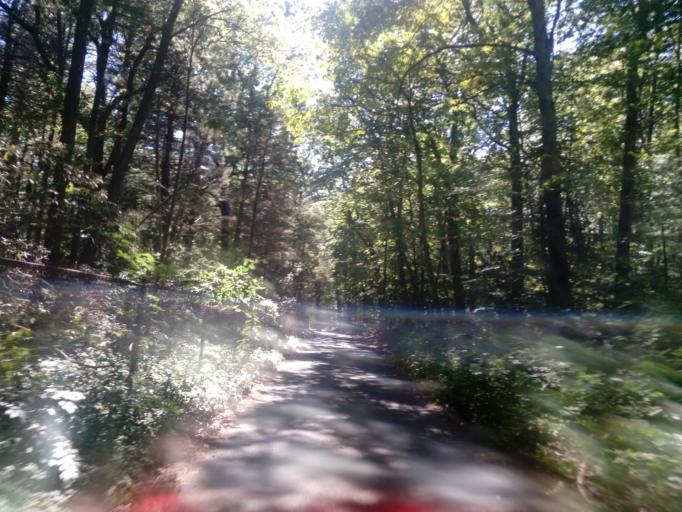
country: US
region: New York
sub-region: Nassau County
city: Upper Brookville
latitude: 40.8518
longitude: -73.5785
